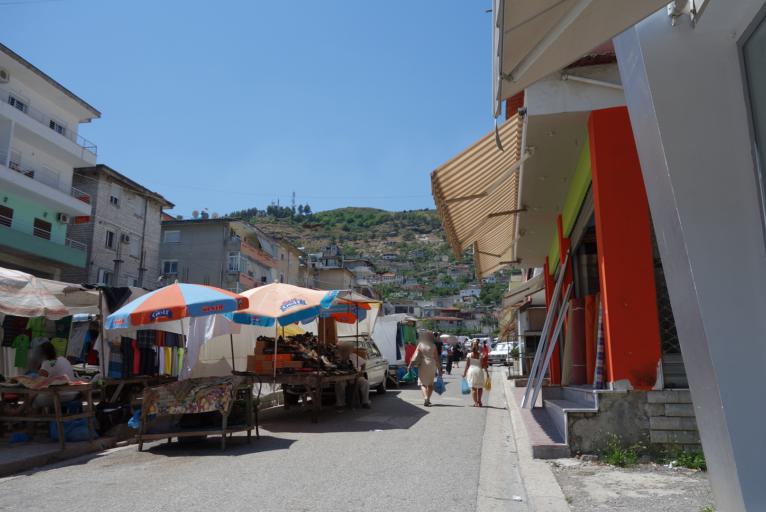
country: AL
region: Gjirokaster
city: Gjirokaster
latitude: 40.0797
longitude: 20.1374
